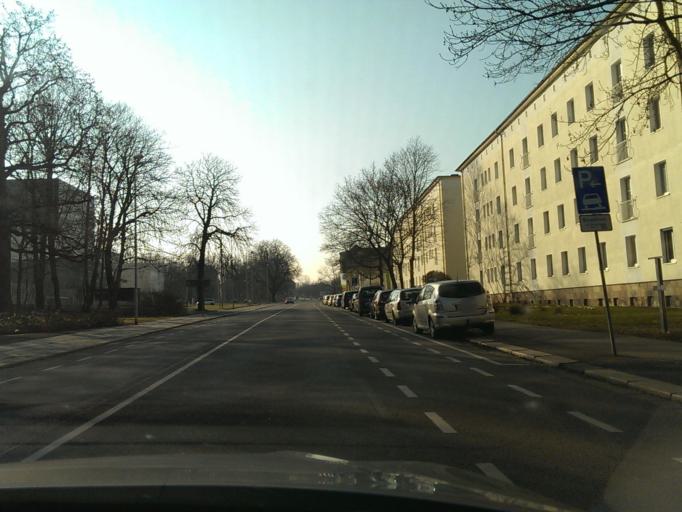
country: DE
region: Saxony
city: Chemnitz
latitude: 50.8298
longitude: 12.9265
